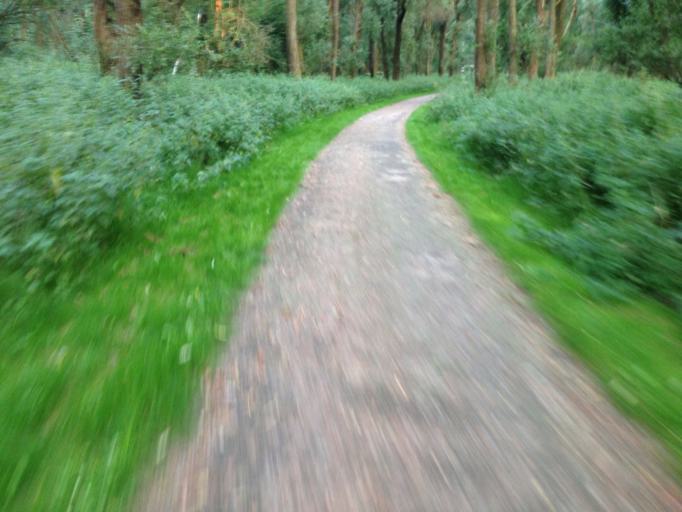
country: NL
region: Flevoland
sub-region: Gemeente Almere
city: Almere Stad
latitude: 52.4114
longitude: 5.2295
